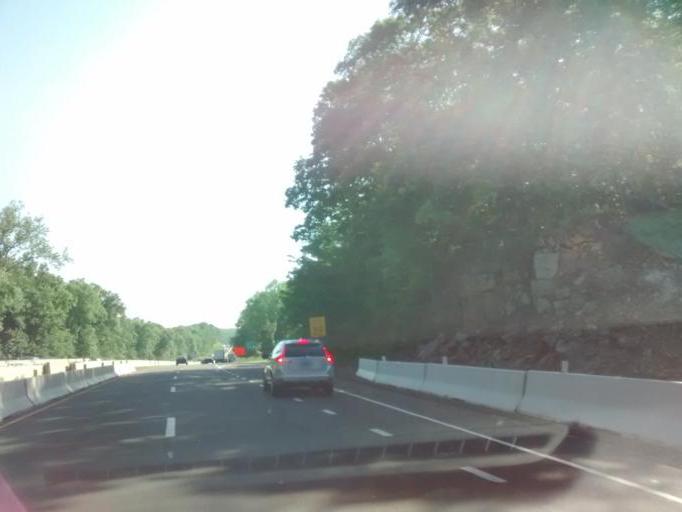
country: US
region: Connecticut
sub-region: New London County
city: Niantic
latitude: 41.3448
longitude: -72.2291
